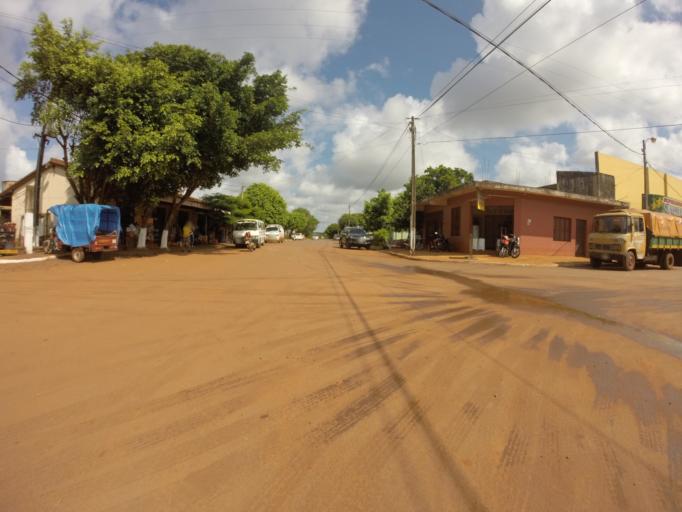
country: PY
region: Alto Parana
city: Ciudad del Este
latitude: -25.4011
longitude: -54.6447
